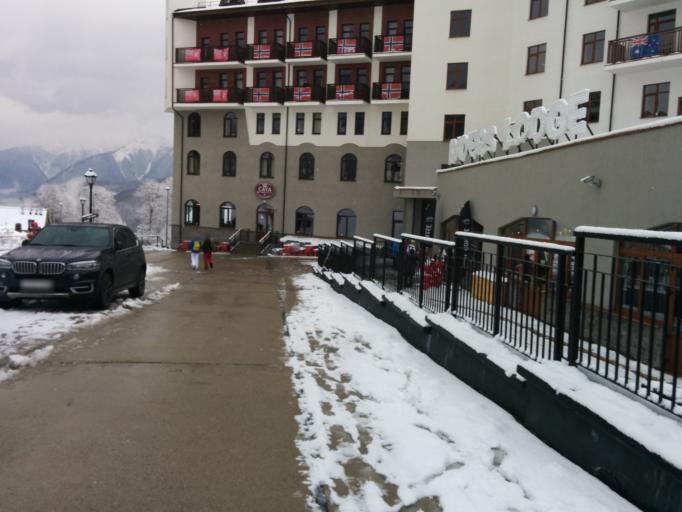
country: RU
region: Krasnodarskiy
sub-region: Sochi City
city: Krasnaya Polyana
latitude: 43.6605
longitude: 40.3201
